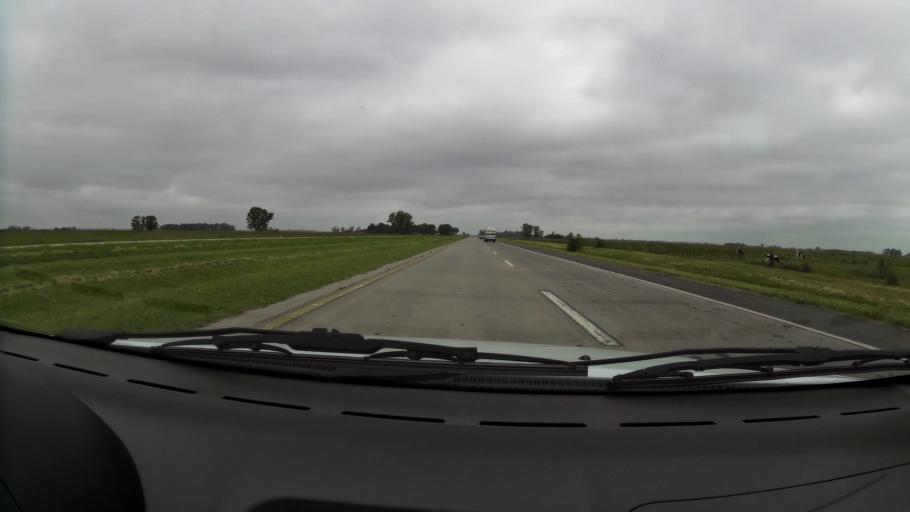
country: AR
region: Buenos Aires
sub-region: Partido de Brandsen
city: Brandsen
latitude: -35.0270
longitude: -58.2141
